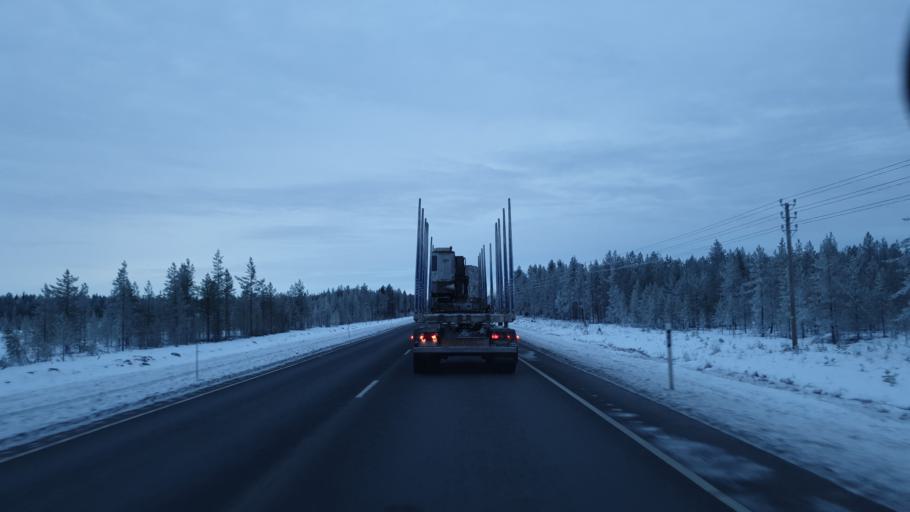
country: FI
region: Northern Ostrobothnia
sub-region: Oulunkaari
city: Ii
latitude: 65.3804
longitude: 25.3771
